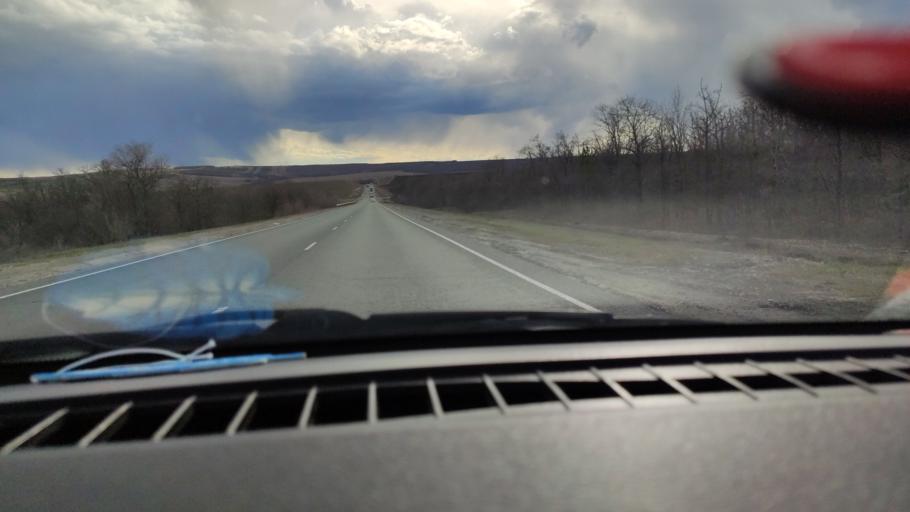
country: RU
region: Saratov
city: Sinodskoye
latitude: 51.9308
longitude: 46.5788
